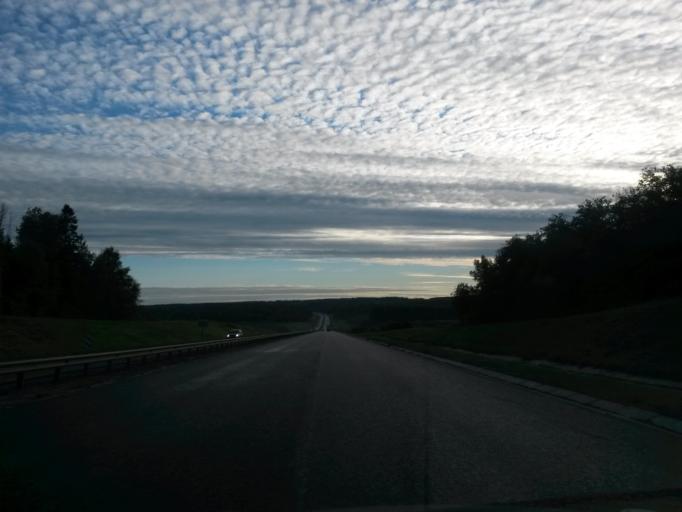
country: RU
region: Vladimir
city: Strunino
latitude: 56.5302
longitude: 38.5745
